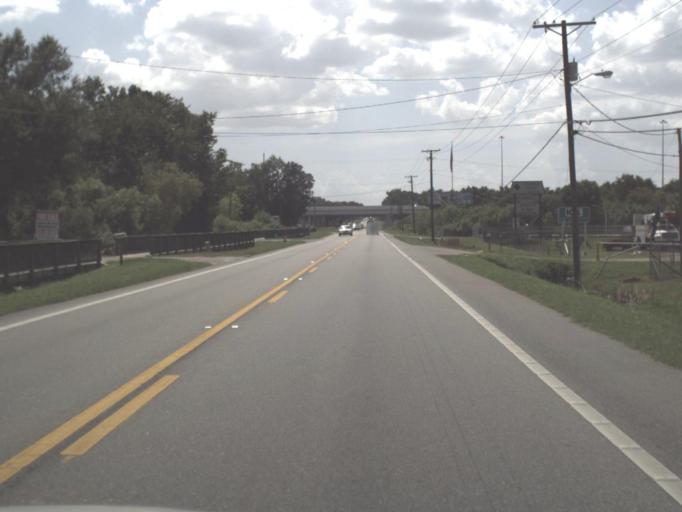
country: US
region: Florida
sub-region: Hillsborough County
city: Mango
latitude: 27.9980
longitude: -82.3224
